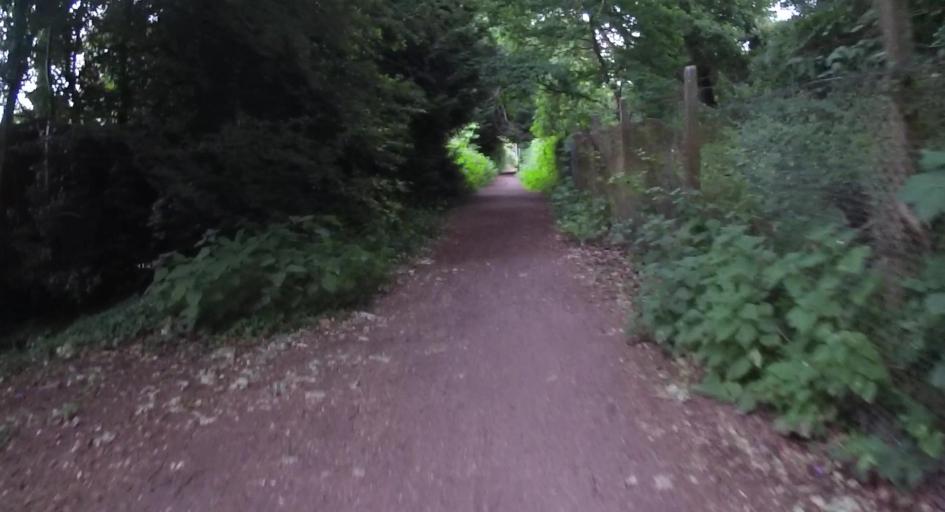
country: GB
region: England
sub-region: Hampshire
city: Farnborough
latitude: 51.2959
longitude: -0.7699
